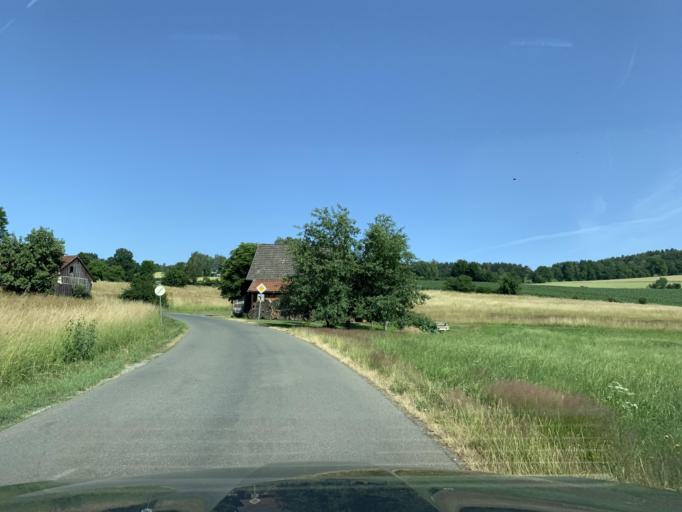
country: DE
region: Bavaria
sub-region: Upper Palatinate
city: Dieterskirchen
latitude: 49.4181
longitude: 12.4296
